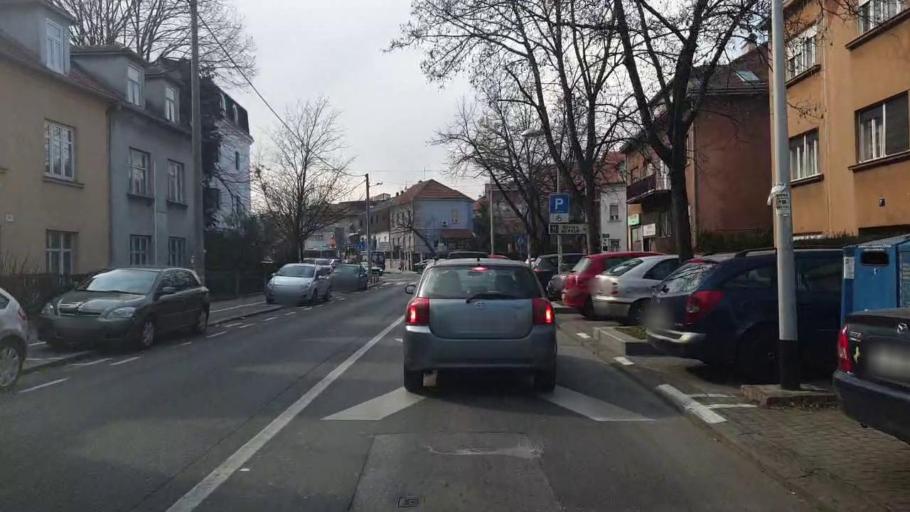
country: HR
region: Grad Zagreb
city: Zagreb
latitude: 45.8179
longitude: 15.9982
